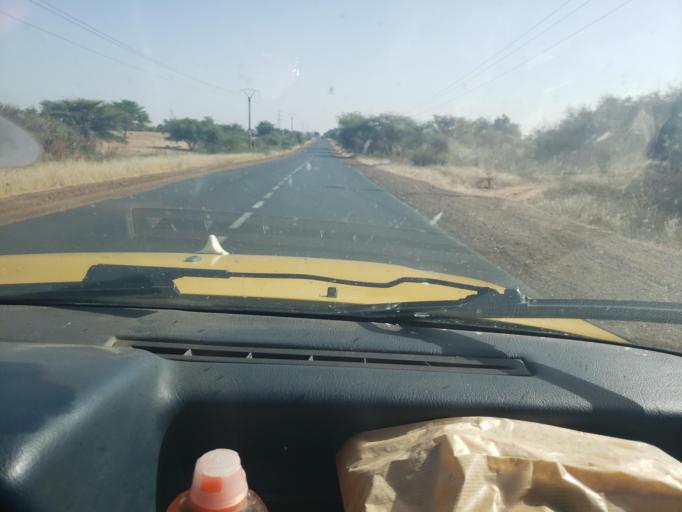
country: SN
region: Louga
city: Louga
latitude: 15.6606
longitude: -16.2578
